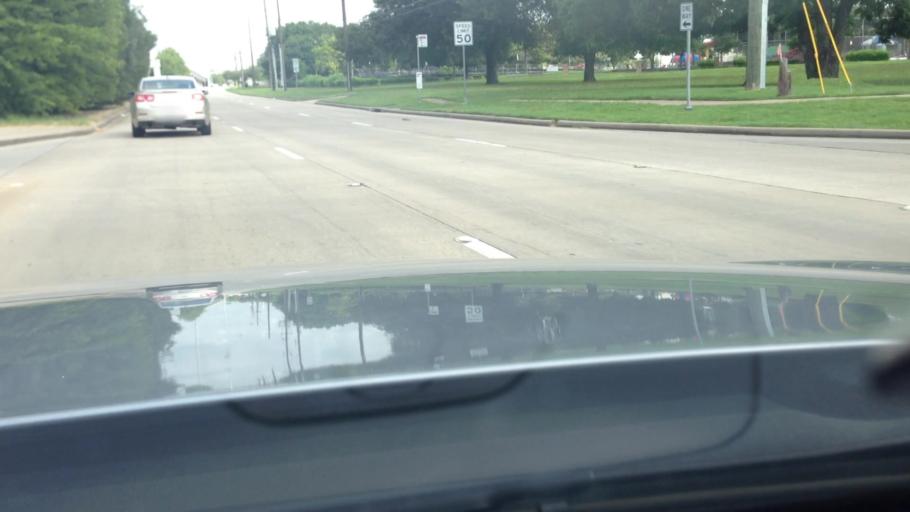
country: US
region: Texas
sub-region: Harris County
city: Hudson
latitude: 29.9536
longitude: -95.5375
